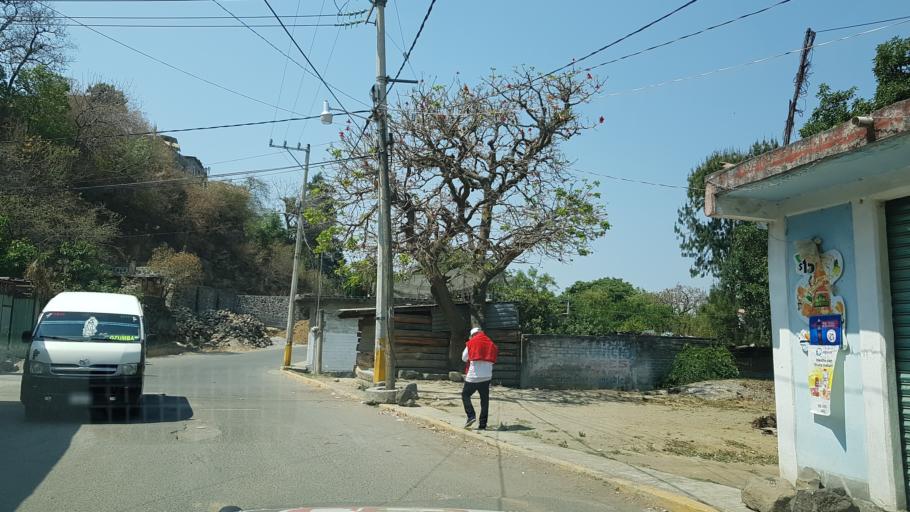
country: MX
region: Mexico
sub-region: Atlautla
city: San Andres Tlalamac
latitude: 18.9650
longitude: -98.8096
